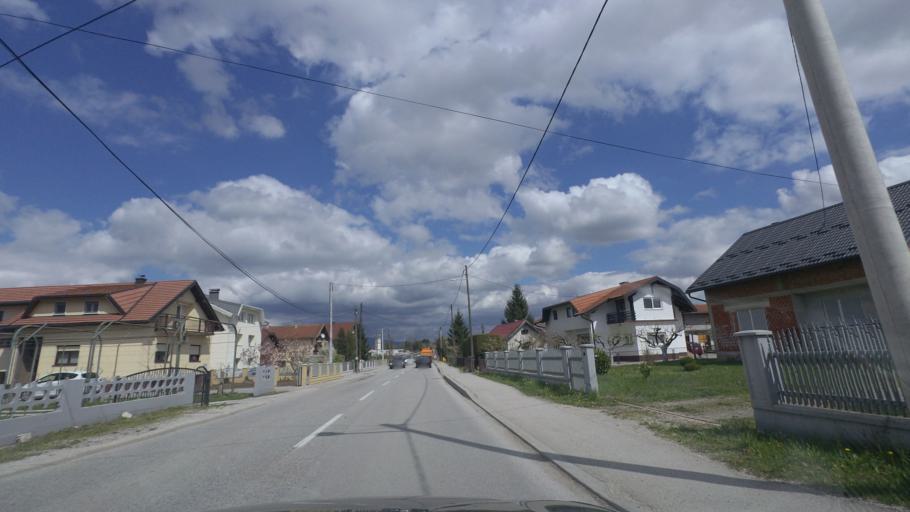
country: HR
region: Zagrebacka
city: Kerestinec
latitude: 45.7717
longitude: 15.8096
